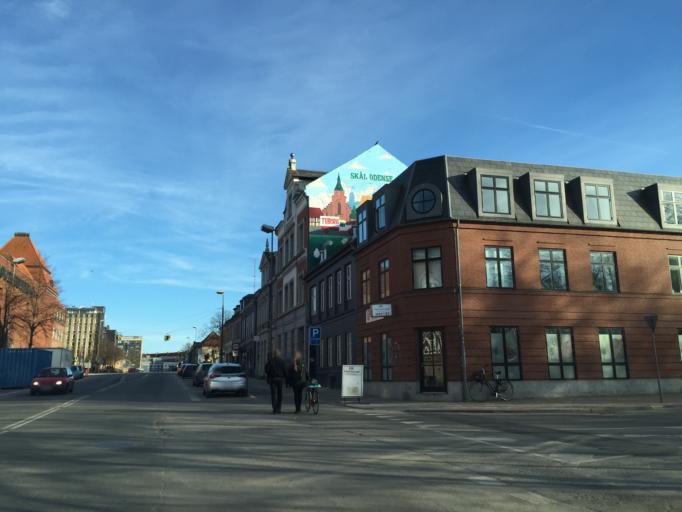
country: DK
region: South Denmark
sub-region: Odense Kommune
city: Odense
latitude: 55.3949
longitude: 10.3930
